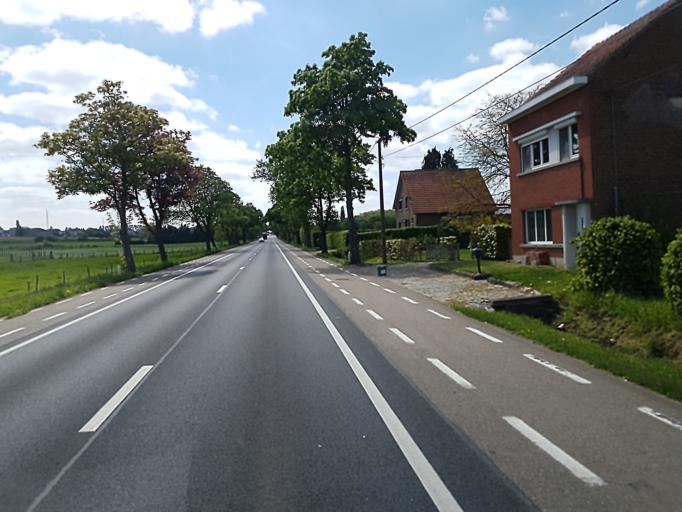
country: BE
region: Flanders
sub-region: Provincie Vlaams-Brabant
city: Glabbeek-Zuurbemde
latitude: 50.8544
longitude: 4.9522
